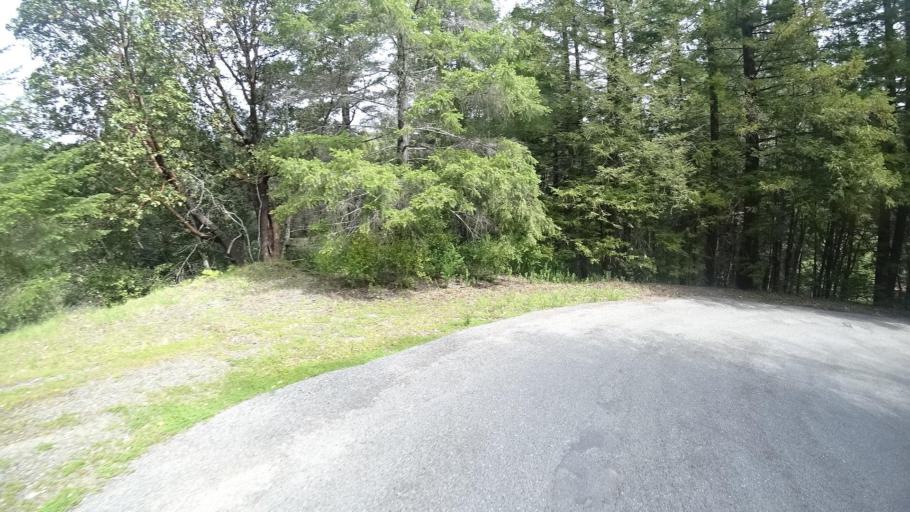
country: US
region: California
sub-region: Humboldt County
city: Redway
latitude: 40.0674
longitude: -123.8317
